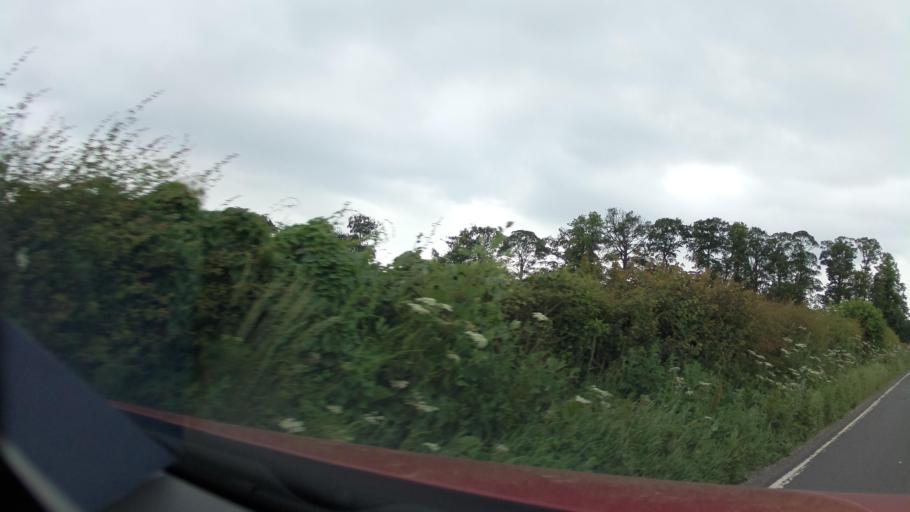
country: GB
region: England
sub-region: Derbyshire
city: Rodsley
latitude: 52.9127
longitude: -1.7609
